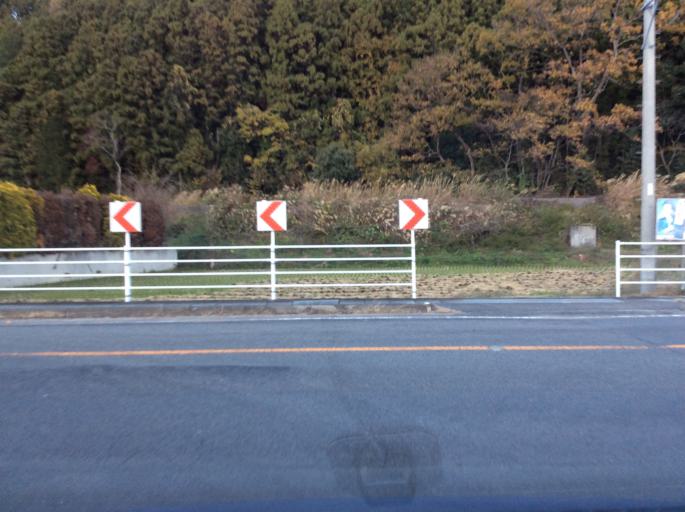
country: JP
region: Fukushima
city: Iwaki
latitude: 37.1366
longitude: 140.8523
